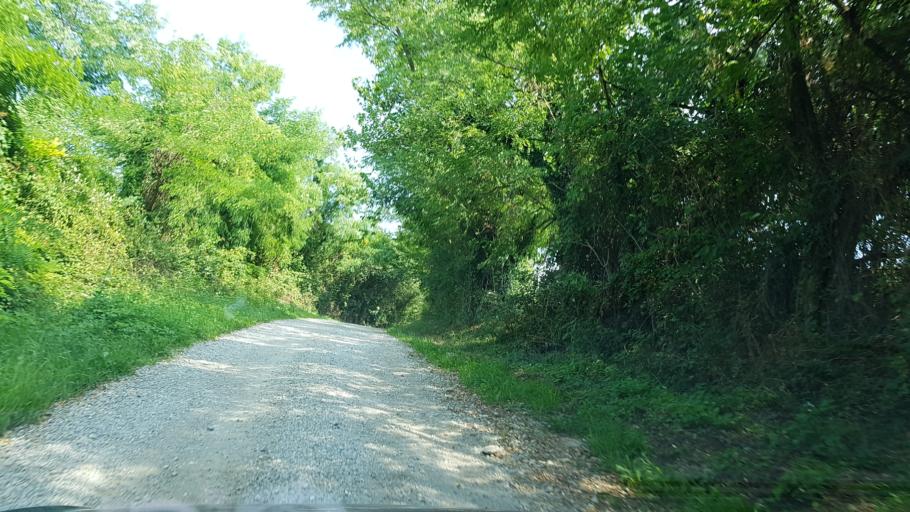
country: SI
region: Brda
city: Dobrovo
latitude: 45.9955
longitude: 13.5153
